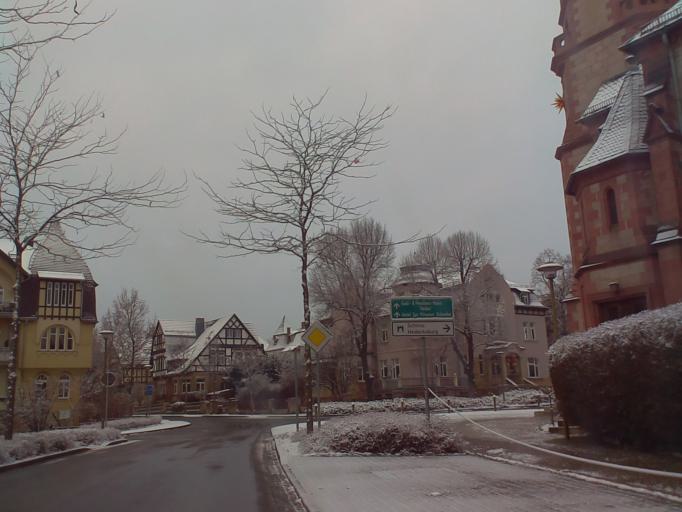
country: DE
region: Thuringia
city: Rudolstadt
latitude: 50.7189
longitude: 11.3284
